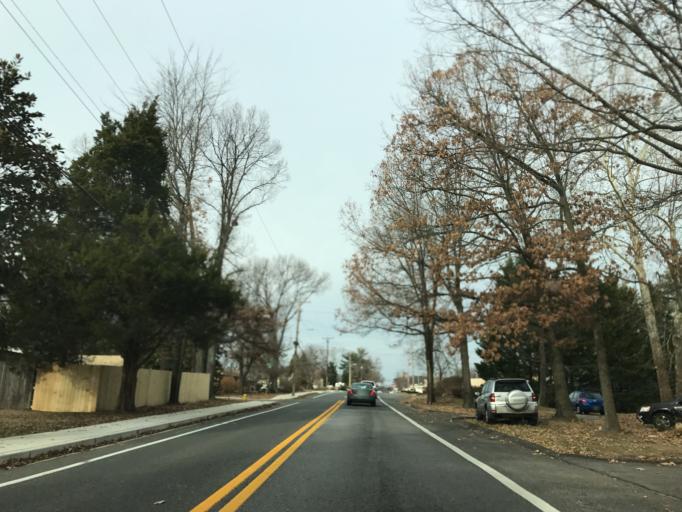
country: US
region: Maryland
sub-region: Anne Arundel County
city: Severna Park
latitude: 39.0763
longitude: -76.5484
